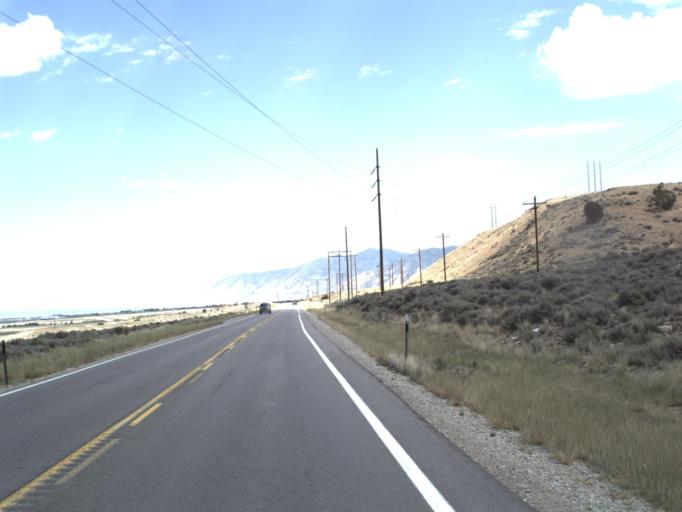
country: US
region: Utah
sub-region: Tooele County
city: Tooele
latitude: 40.4692
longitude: -112.3516
